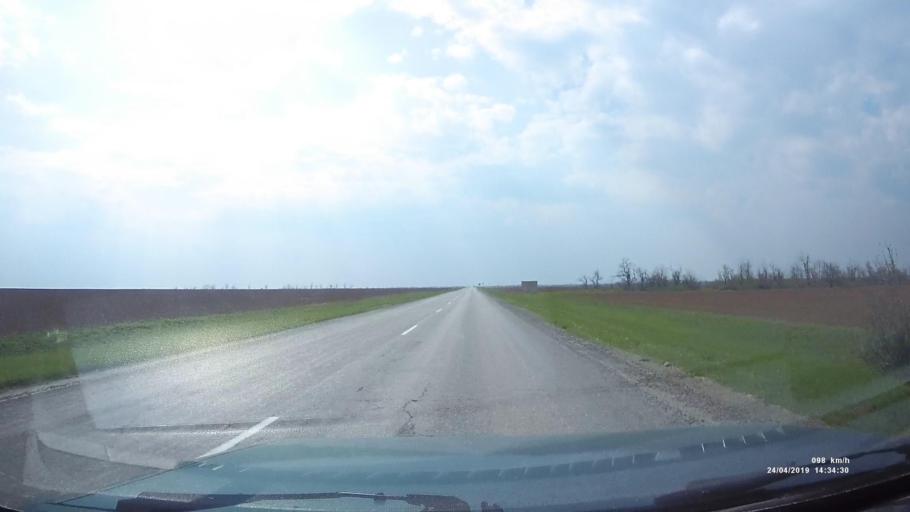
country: RU
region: Kalmykiya
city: Arshan'
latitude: 46.3737
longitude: 43.9306
